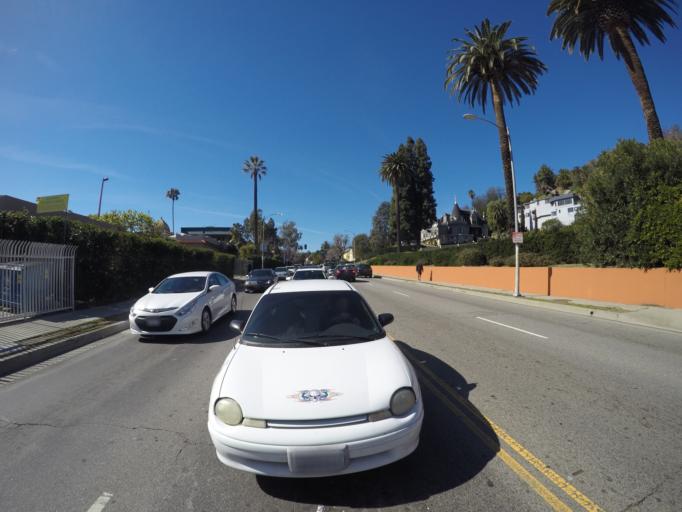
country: US
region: California
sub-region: Los Angeles County
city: Hollywood
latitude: 34.1041
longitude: -118.3408
